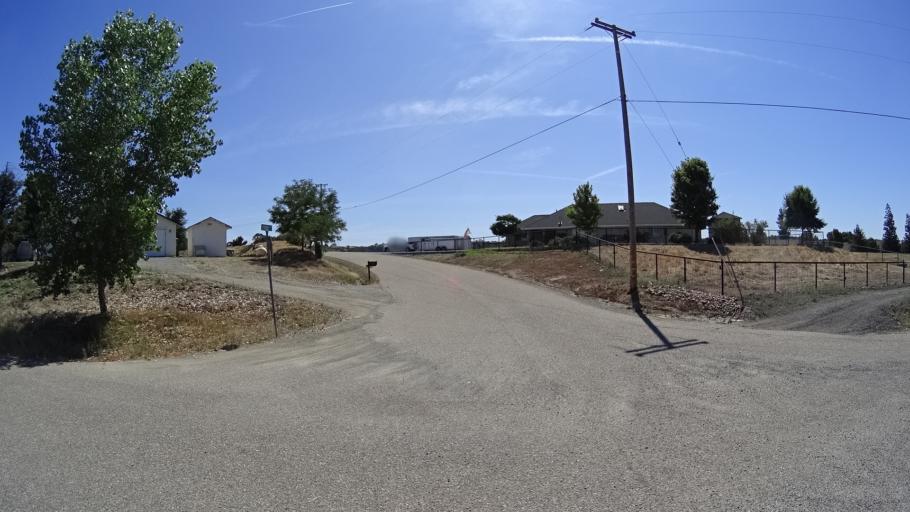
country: US
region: California
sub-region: Calaveras County
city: Rancho Calaveras
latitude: 38.1563
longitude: -120.8949
